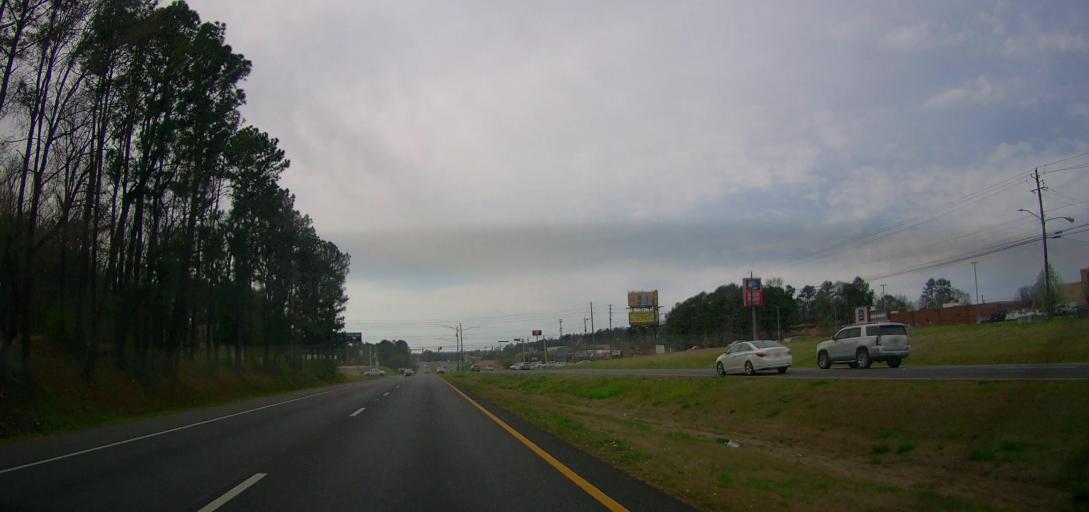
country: US
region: Alabama
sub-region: Walker County
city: Jasper
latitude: 33.8456
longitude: -87.2572
